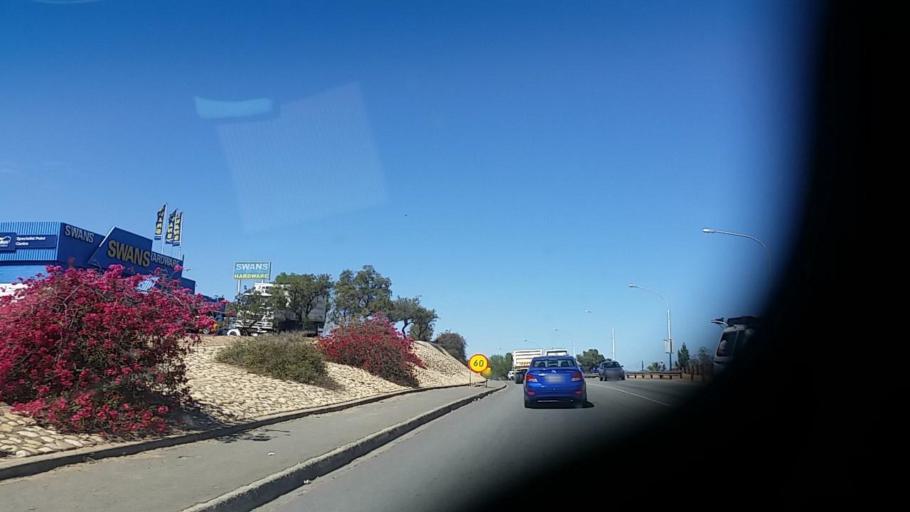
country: ZA
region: Western Cape
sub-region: Eden District Municipality
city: Oudtshoorn
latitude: -33.5947
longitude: 22.2163
